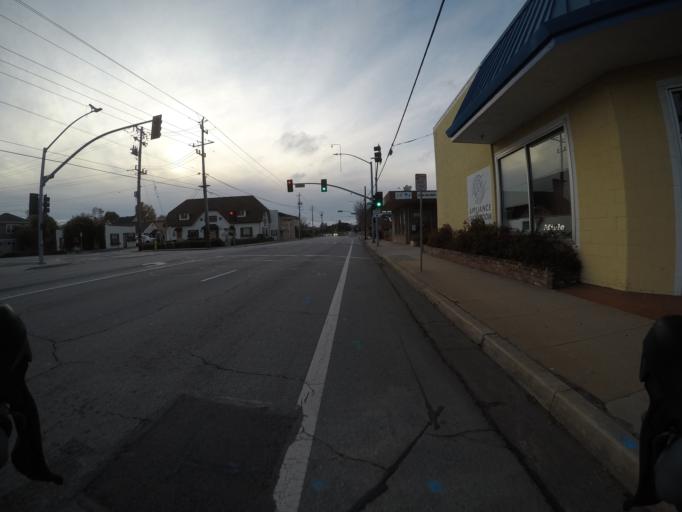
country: US
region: California
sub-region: Santa Cruz County
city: Twin Lakes
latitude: 36.9816
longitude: -122.0046
